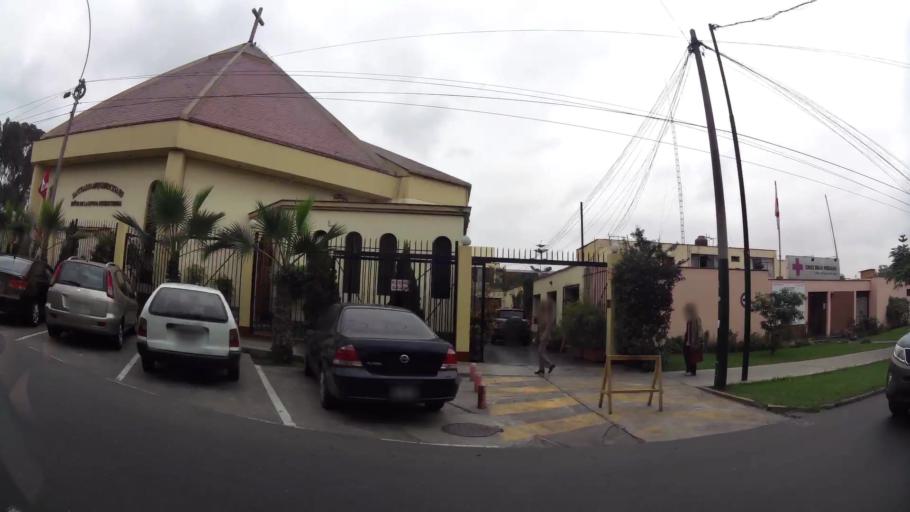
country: PE
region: Lima
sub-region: Lima
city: Surco
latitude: -12.1325
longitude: -76.9828
